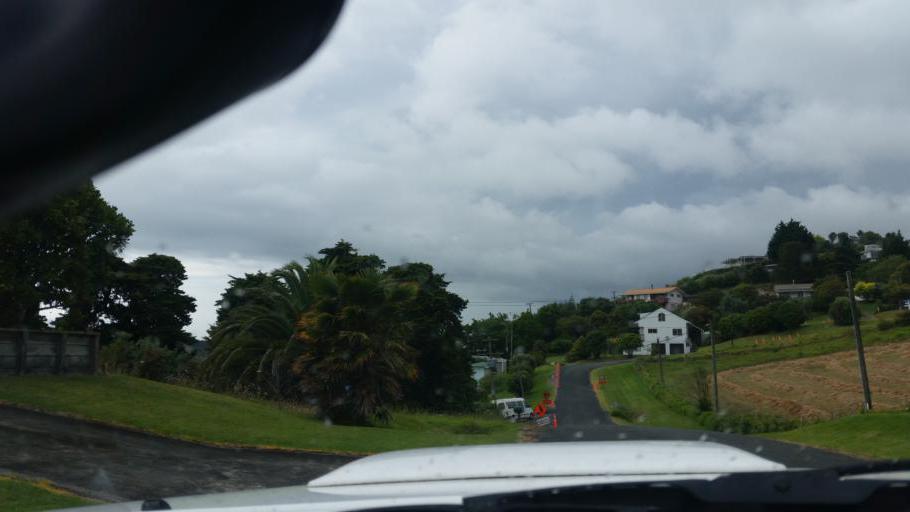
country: NZ
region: Auckland
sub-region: Auckland
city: Wellsford
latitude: -36.1537
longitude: 174.2267
